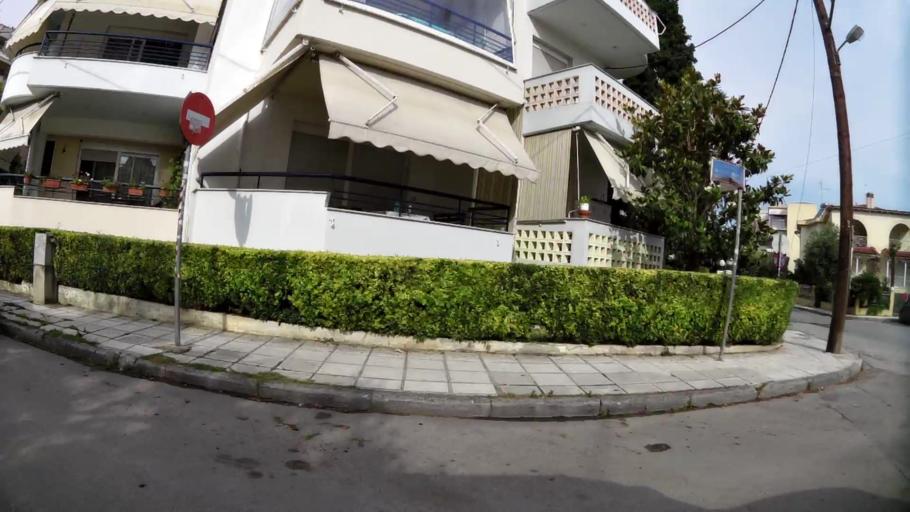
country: GR
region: Central Macedonia
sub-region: Nomos Thessalonikis
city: Thermi
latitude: 40.5459
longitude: 23.0169
